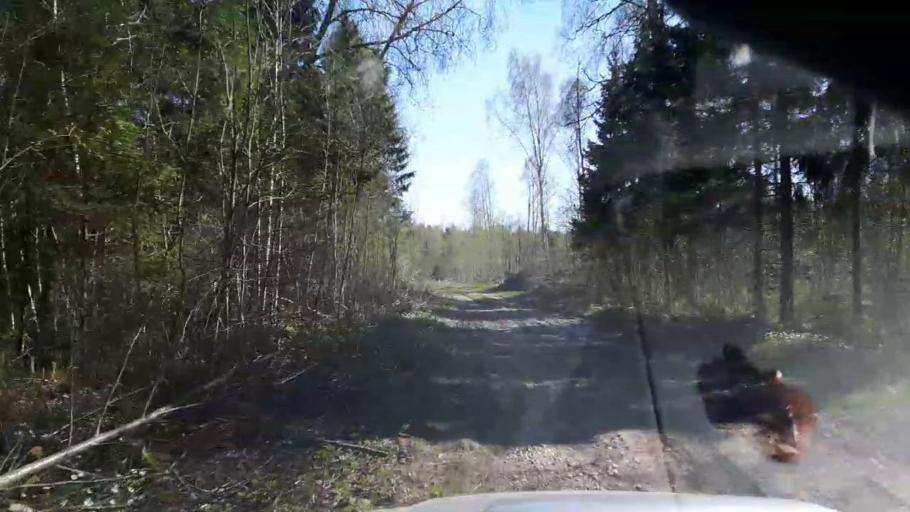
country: EE
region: Paernumaa
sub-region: Tootsi vald
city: Tootsi
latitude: 58.5436
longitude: 24.8025
